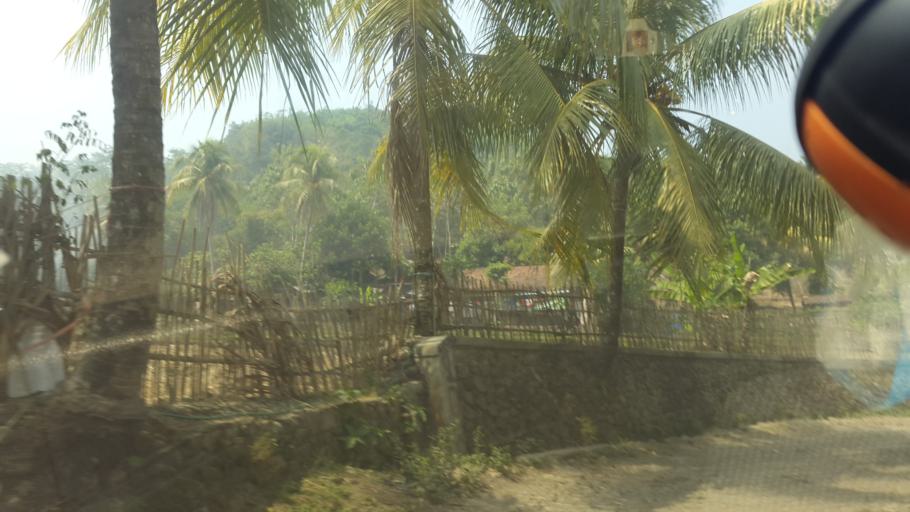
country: ID
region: West Java
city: Rancagadog
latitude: -7.0099
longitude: 106.7093
